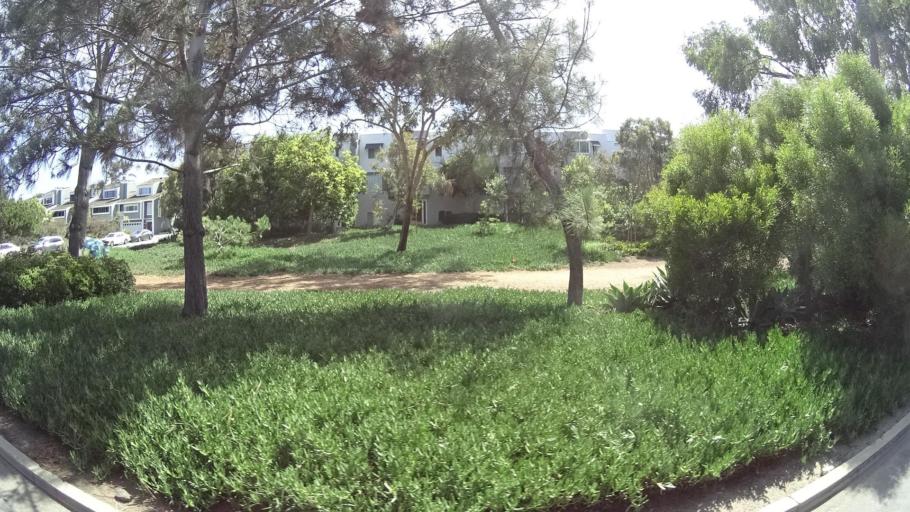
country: US
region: California
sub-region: Los Angeles County
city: Hermosa Beach
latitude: 33.8553
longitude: -118.3945
